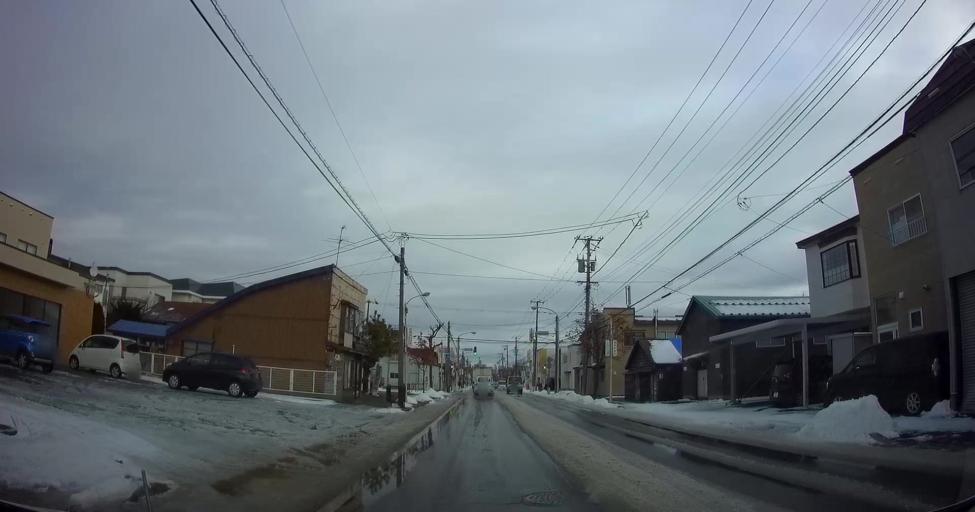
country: JP
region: Hokkaido
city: Hakodate
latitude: 41.7779
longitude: 140.7454
